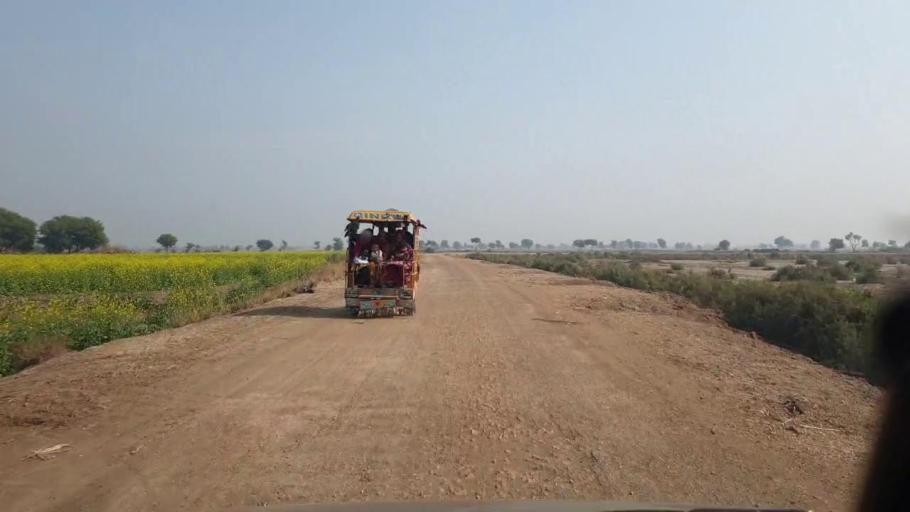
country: PK
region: Sindh
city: Shahdadpur
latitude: 26.0412
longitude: 68.4904
